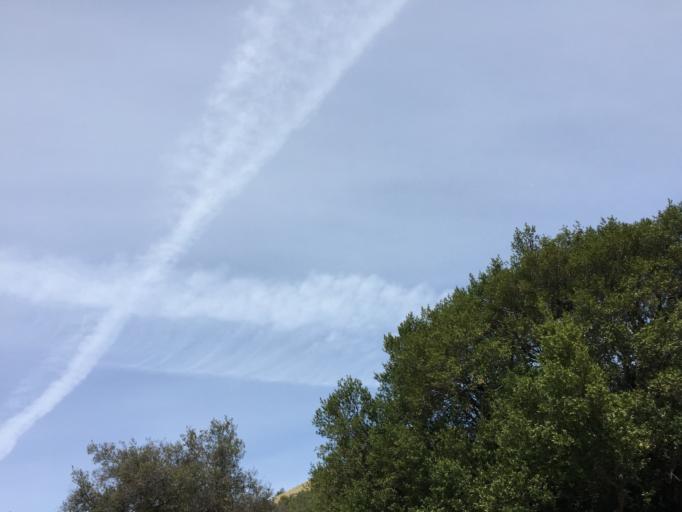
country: US
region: California
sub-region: Contra Costa County
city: Diablo
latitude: 37.8766
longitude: -121.9308
